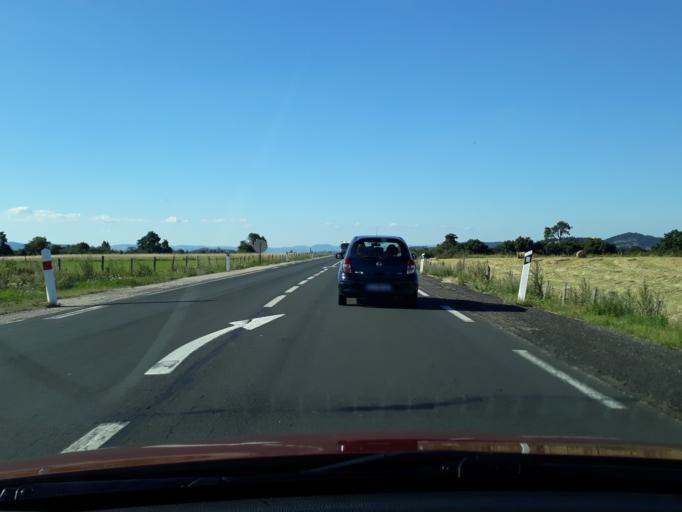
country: FR
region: Auvergne
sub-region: Departement de la Haute-Loire
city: Solignac-sur-Loire
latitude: 44.9054
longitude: 3.8505
